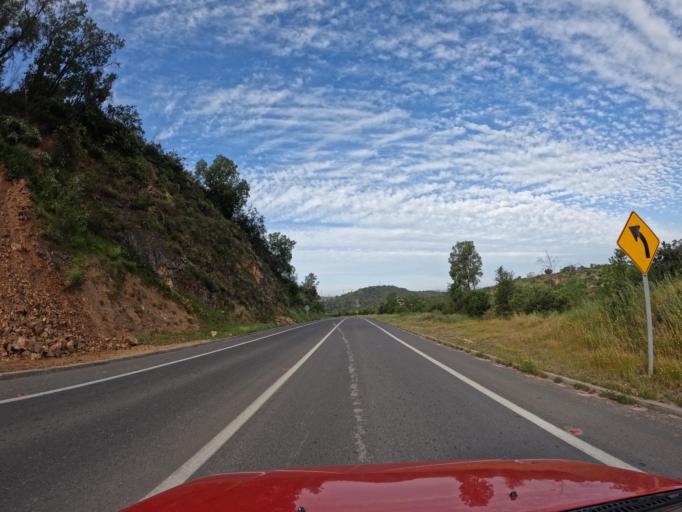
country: CL
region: Valparaiso
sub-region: San Antonio Province
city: San Antonio
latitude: -34.0476
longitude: -71.5949
